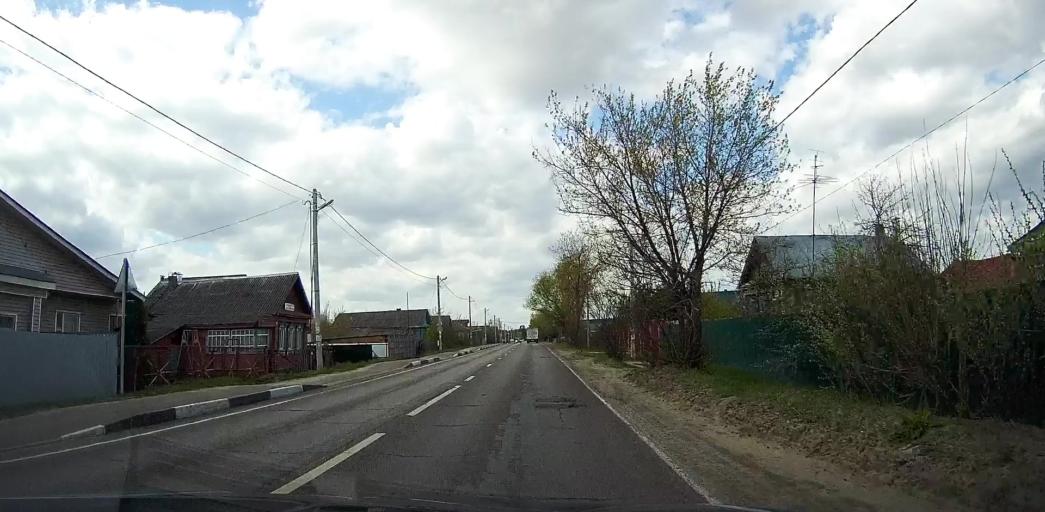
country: RU
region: Moskovskaya
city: Davydovo
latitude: 55.6375
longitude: 38.8667
